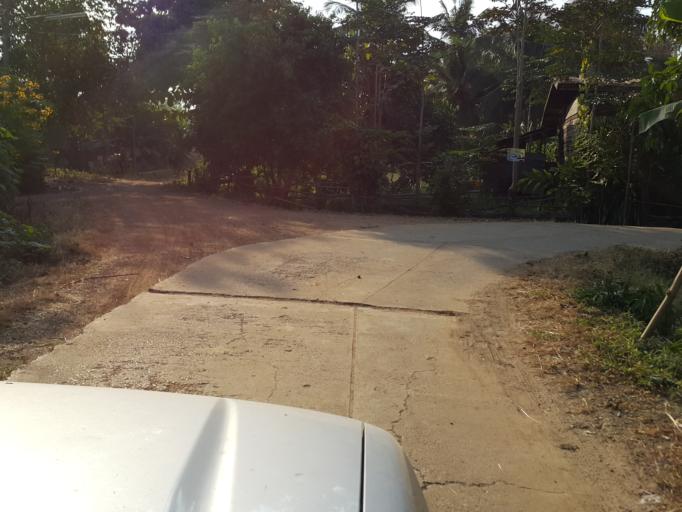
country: TH
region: Sukhothai
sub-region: Amphoe Si Satchanalai
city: Si Satchanalai
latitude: 17.4705
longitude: 99.6476
